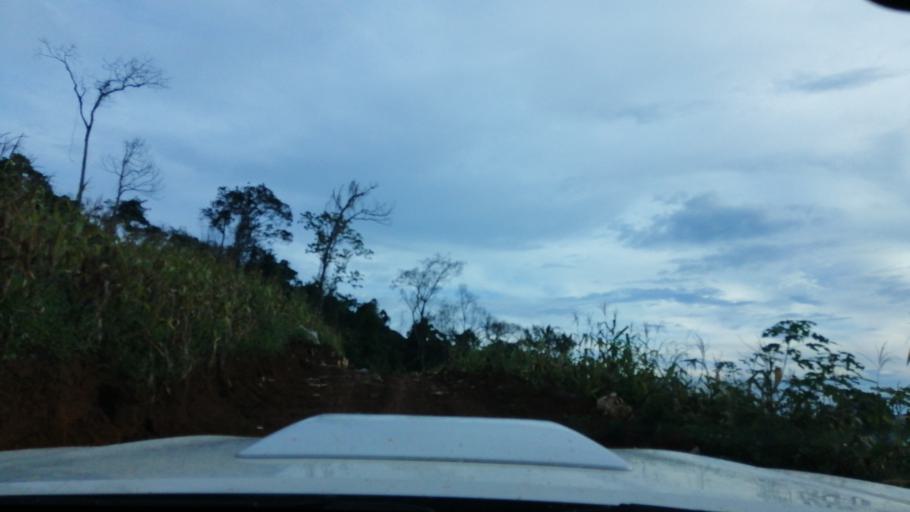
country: TH
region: Nan
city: Chaloem Phra Kiat
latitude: 19.7643
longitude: 101.1202
